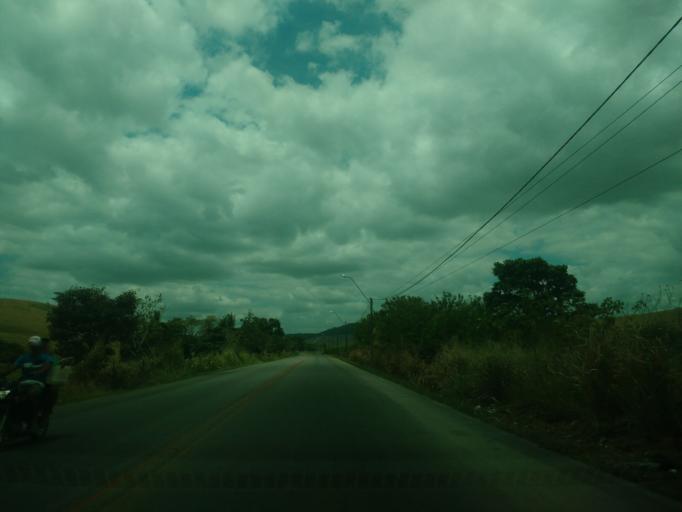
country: BR
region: Alagoas
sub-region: Uniao Dos Palmares
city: Uniao dos Palmares
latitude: -9.1533
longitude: -36.0363
